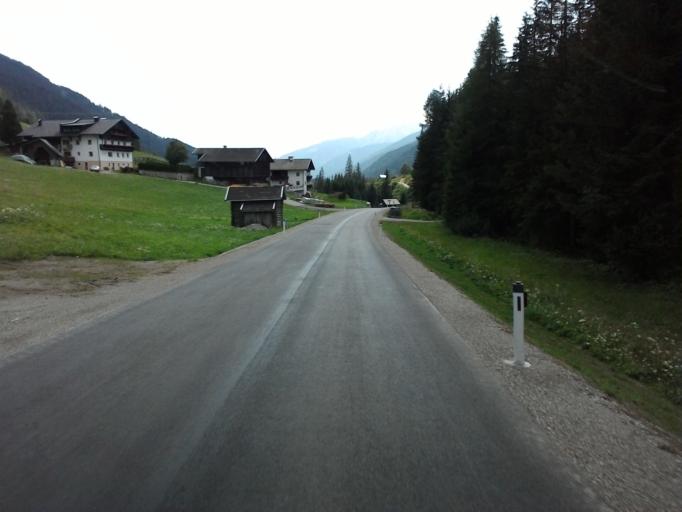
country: AT
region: Tyrol
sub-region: Politischer Bezirk Lienz
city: Abfaltersbach
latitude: 46.7151
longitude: 12.5598
